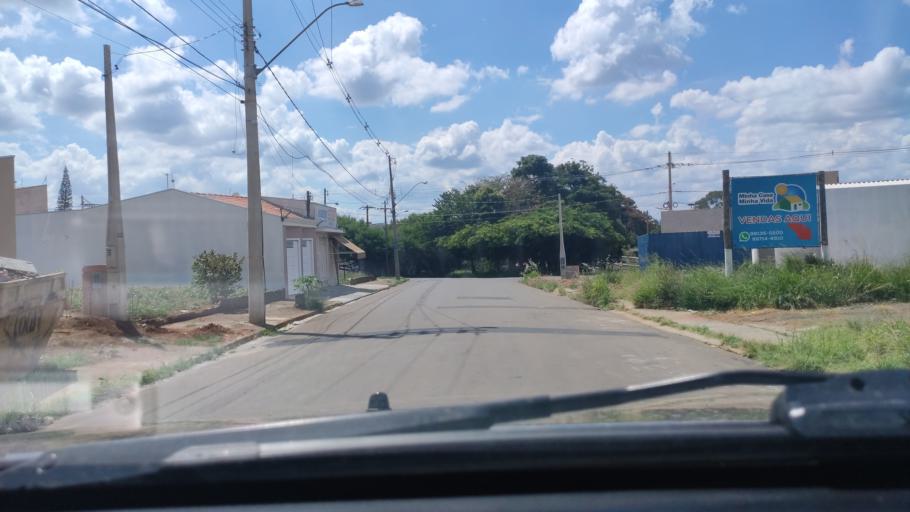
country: BR
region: Sao Paulo
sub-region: Sao Carlos
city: Sao Carlos
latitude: -21.9972
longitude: -47.8781
